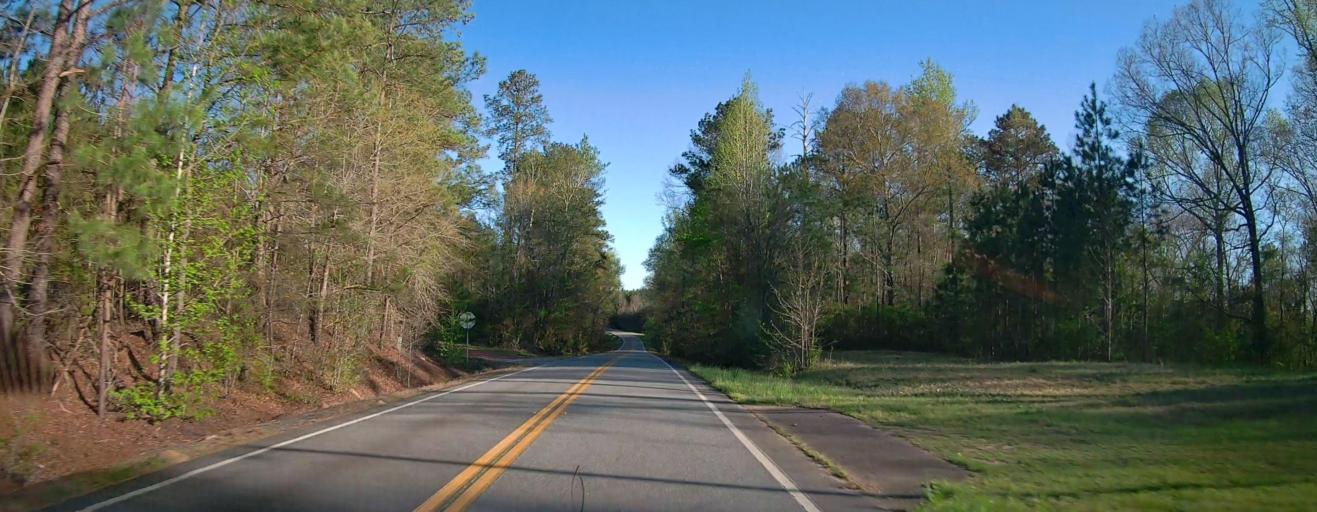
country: US
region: Georgia
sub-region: Baldwin County
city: Hardwick
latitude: 32.9481
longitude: -83.1640
